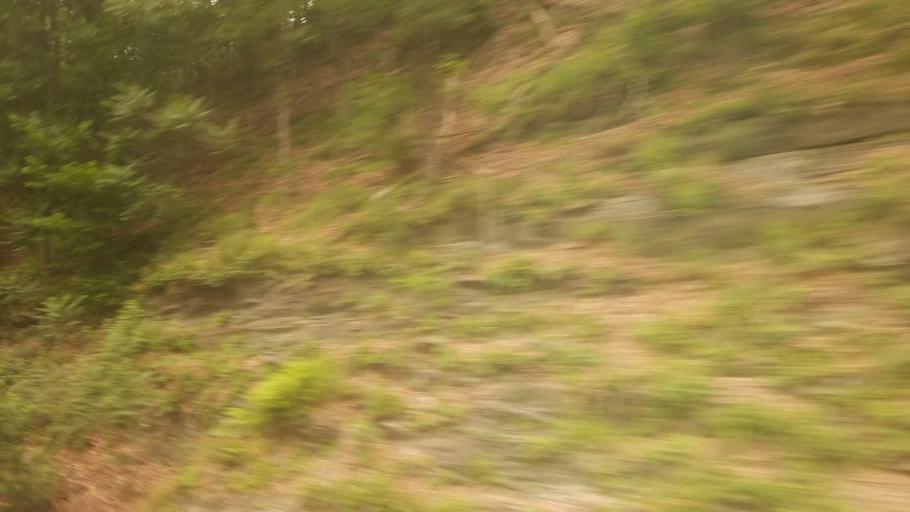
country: US
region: West Virginia
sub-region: Morgan County
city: Berkeley Springs
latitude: 39.6034
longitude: -78.3947
